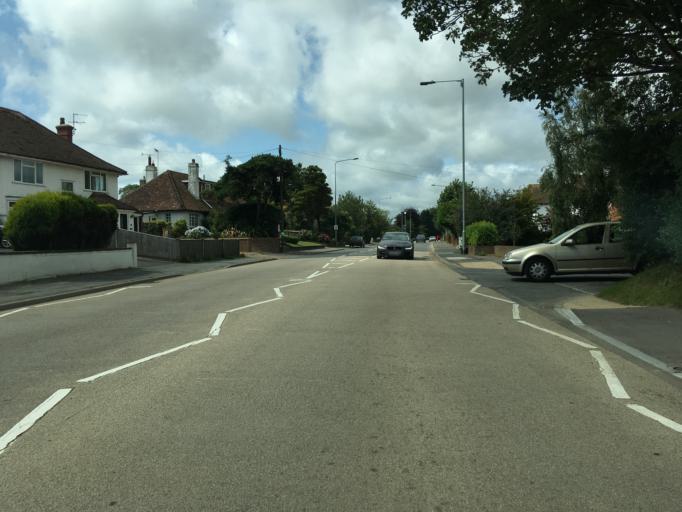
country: GB
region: England
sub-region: East Sussex
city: Bexhill-on-Sea
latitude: 50.8449
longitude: 0.4267
